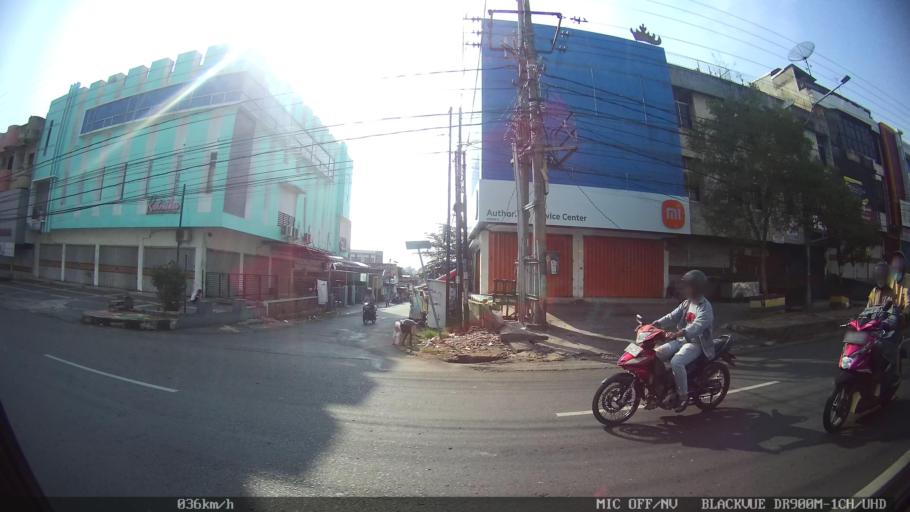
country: ID
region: Lampung
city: Bandarlampung
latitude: -5.4174
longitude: 105.2539
